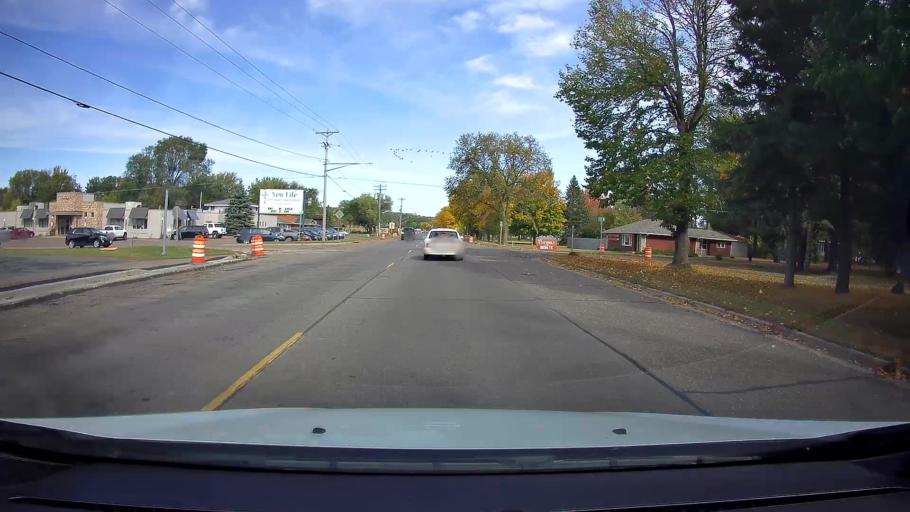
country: US
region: Wisconsin
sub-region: Polk County
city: Saint Croix Falls
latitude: 45.3563
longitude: -92.6370
